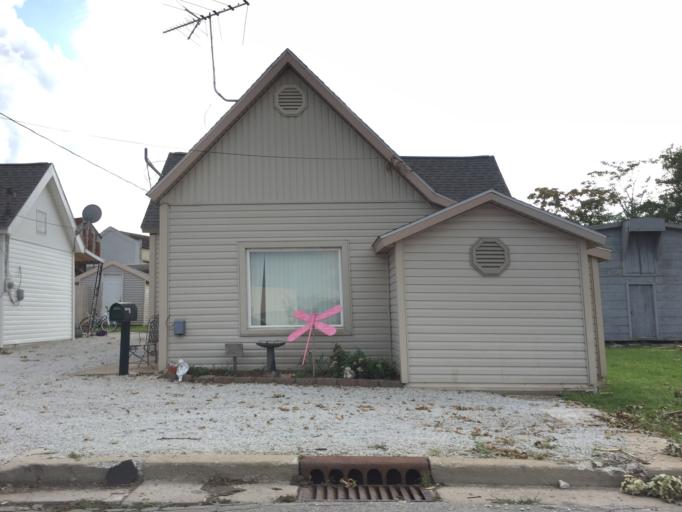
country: US
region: Indiana
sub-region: Howard County
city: Kokomo
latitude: 40.4683
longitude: -86.1252
